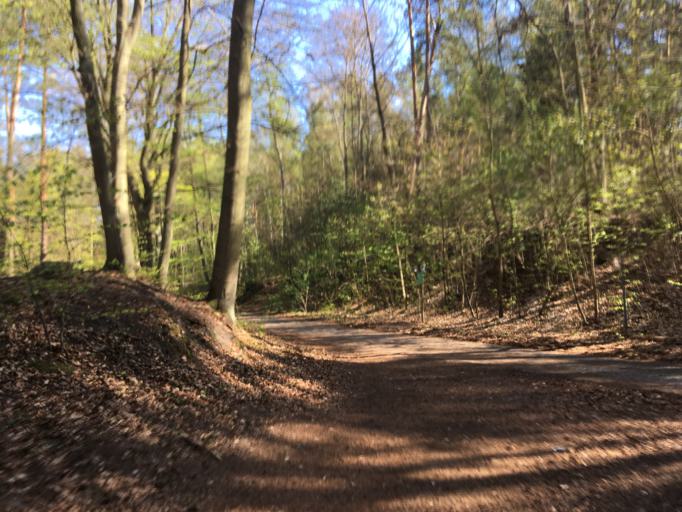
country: DE
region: Brandenburg
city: Wandlitz
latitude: 52.7552
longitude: 13.5333
